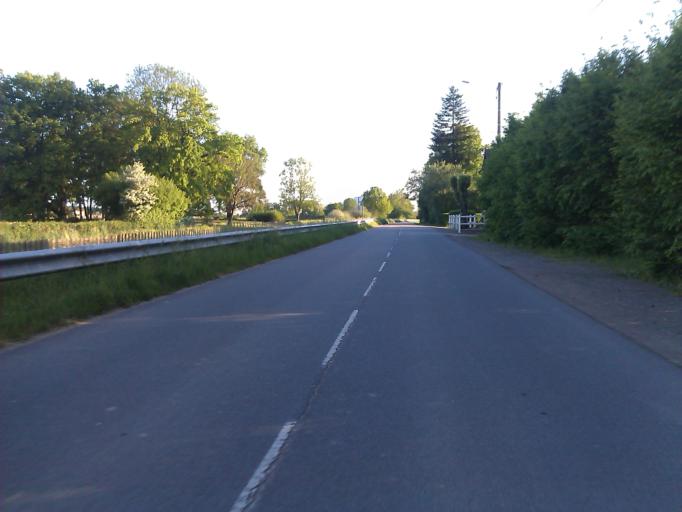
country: FR
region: Bourgogne
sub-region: Departement de Saone-et-Loire
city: Palinges
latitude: 46.5539
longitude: 4.2140
